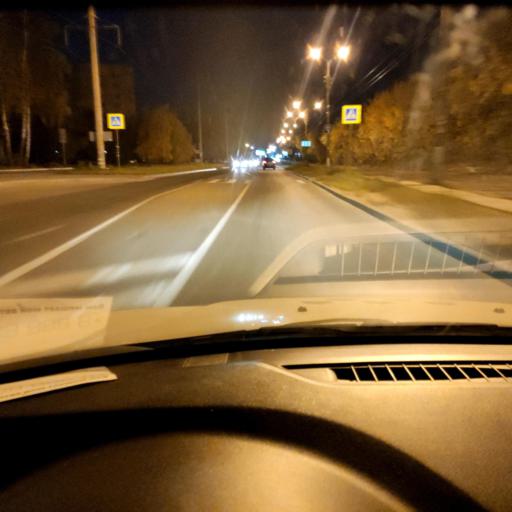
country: RU
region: Samara
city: Tol'yatti
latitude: 53.5276
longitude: 49.3963
